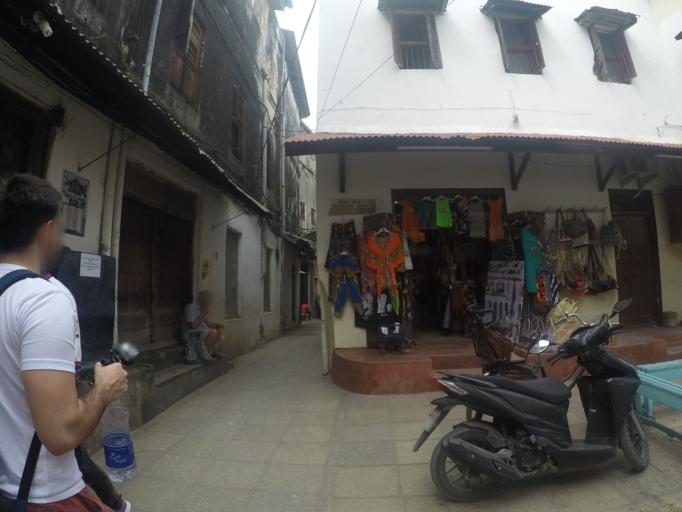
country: TZ
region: Zanzibar Urban/West
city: Zanzibar
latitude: -6.1633
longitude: 39.1899
